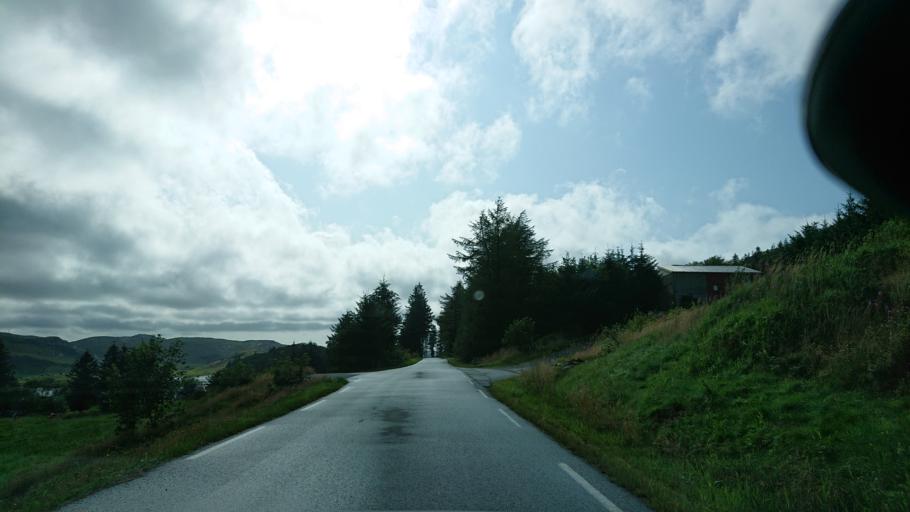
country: NO
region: Rogaland
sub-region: Gjesdal
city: Algard
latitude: 58.6839
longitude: 5.8644
